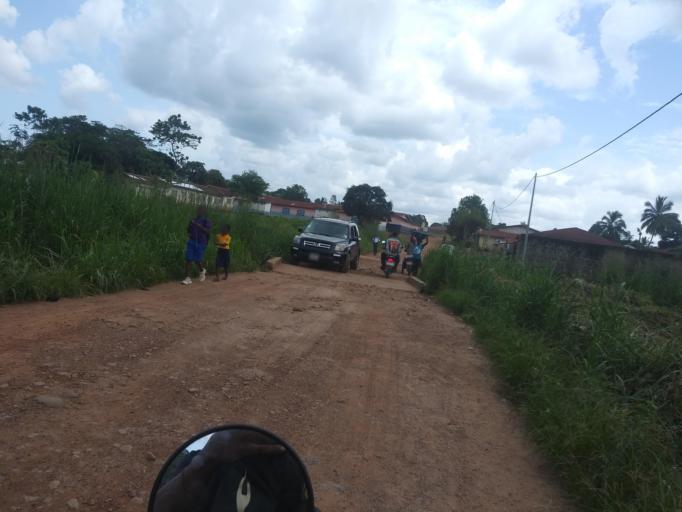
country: SL
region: Northern Province
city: Makeni
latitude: 8.8766
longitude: -12.0434
